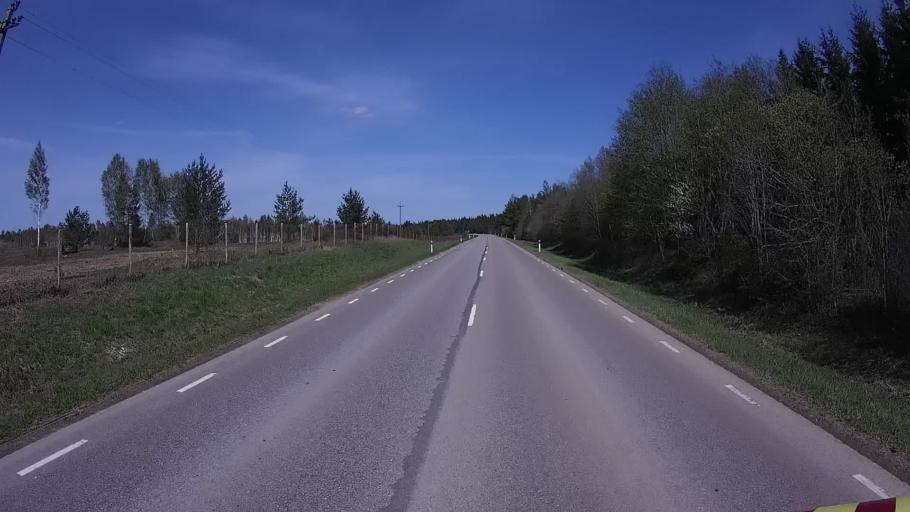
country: EE
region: Harju
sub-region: Keila linn
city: Keila
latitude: 59.3224
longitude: 24.3241
